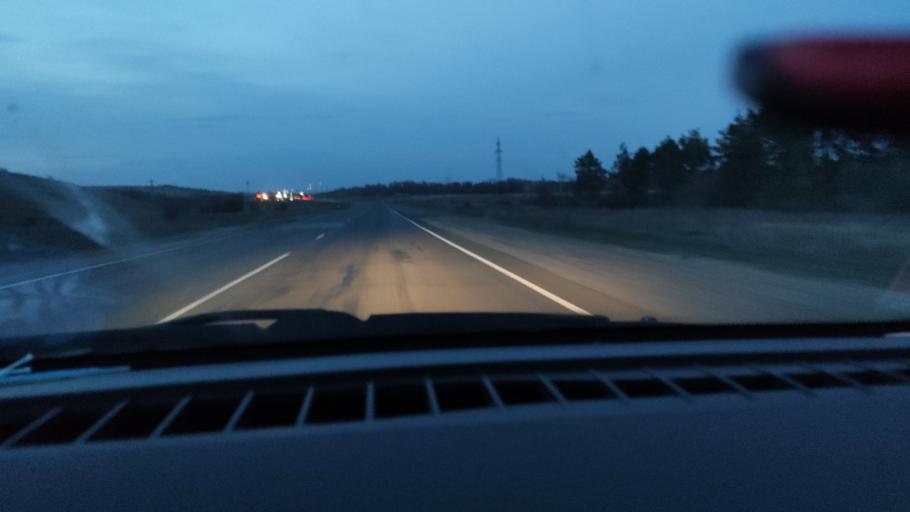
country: RU
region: Saratov
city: Sinodskoye
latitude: 52.0806
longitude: 46.7950
